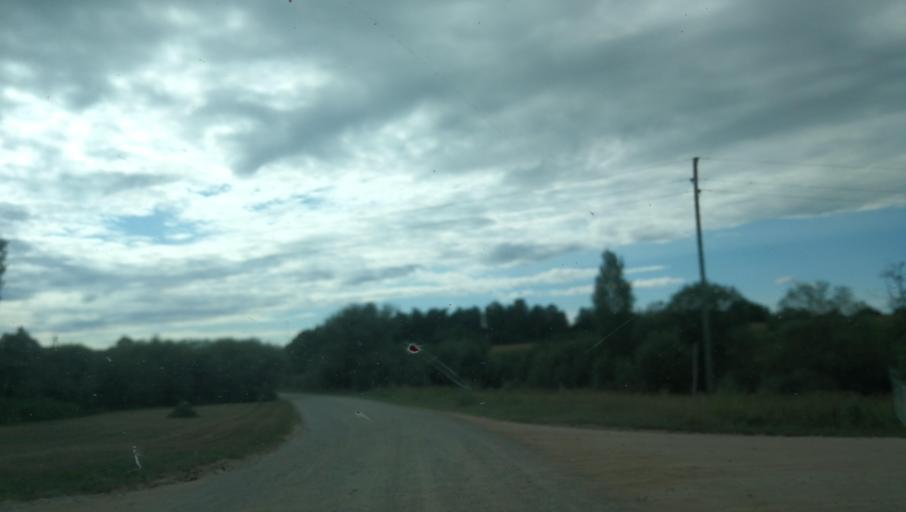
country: LV
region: Cesu Rajons
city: Cesis
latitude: 57.3218
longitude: 25.2751
